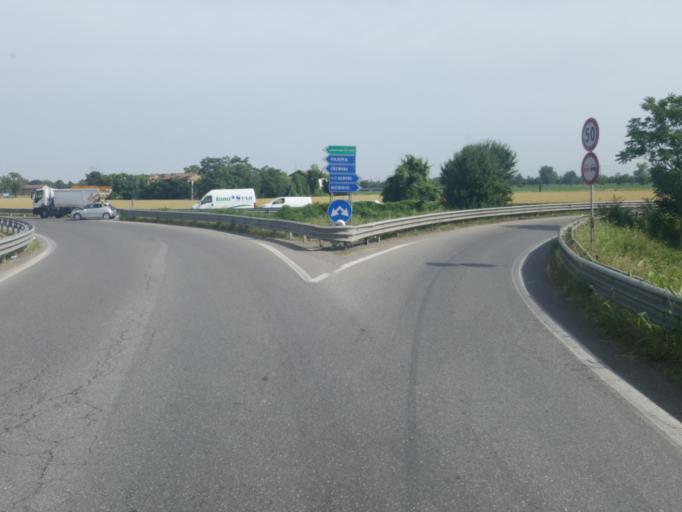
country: IT
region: Emilia-Romagna
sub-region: Provincia di Piacenza
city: Piacenza
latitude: 45.0281
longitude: 9.6817
